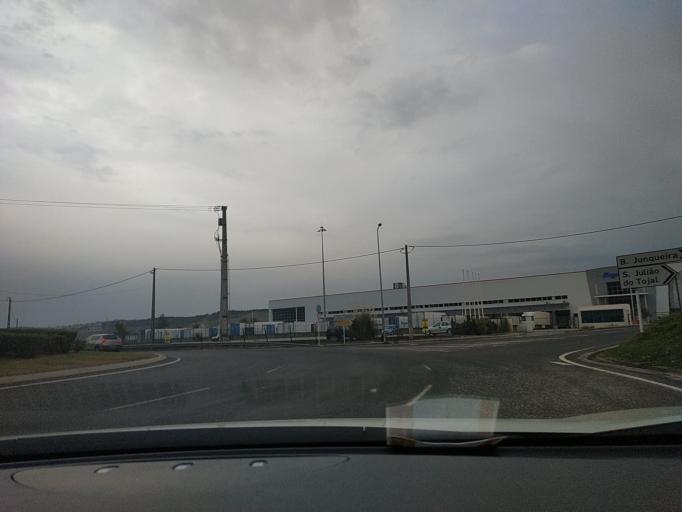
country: PT
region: Lisbon
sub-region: Loures
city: Santo Antao do Tojal
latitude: 38.8611
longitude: -9.1234
